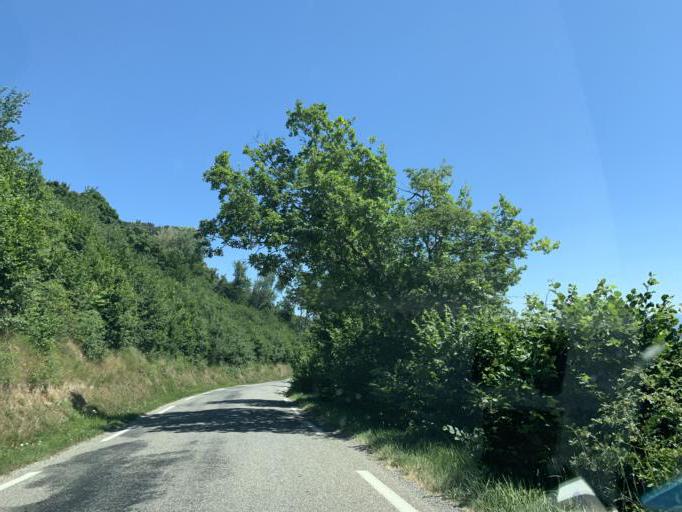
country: FR
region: Provence-Alpes-Cote d'Azur
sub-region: Departement des Hautes-Alpes
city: La Batie-Neuve
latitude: 44.6021
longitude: 6.1440
